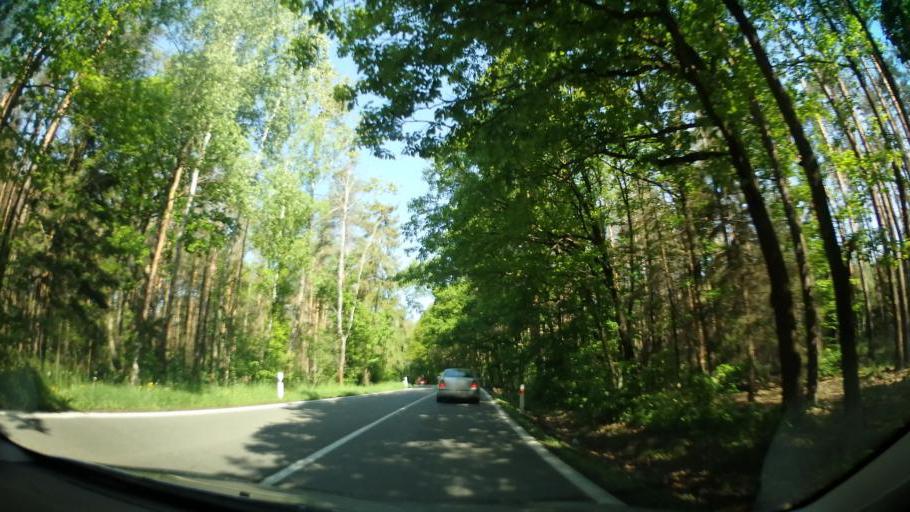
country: CZ
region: South Moravian
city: Zastavka
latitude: 49.1842
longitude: 16.3368
